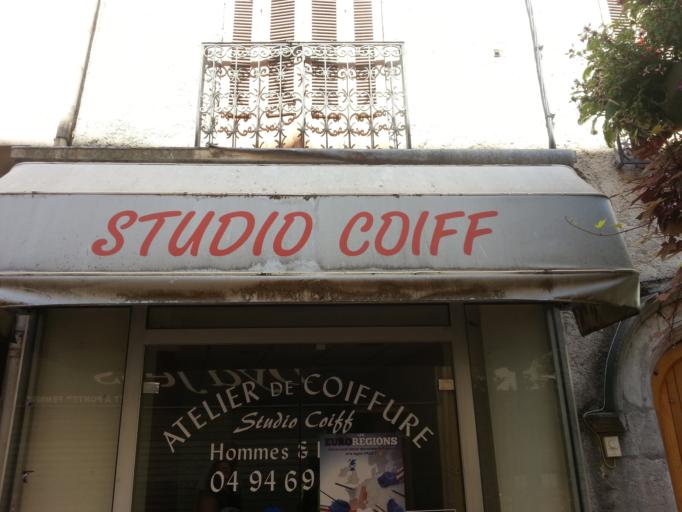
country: FR
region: Provence-Alpes-Cote d'Azur
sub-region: Departement du Var
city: Brignoles
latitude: 43.4068
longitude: 6.0627
